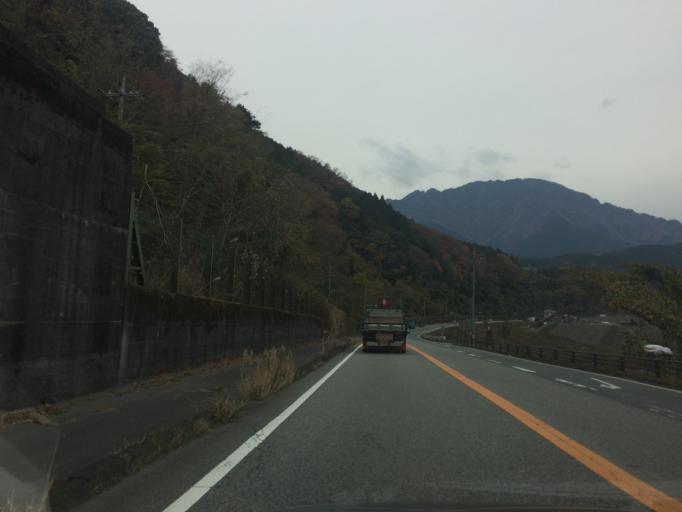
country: JP
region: Shizuoka
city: Fujinomiya
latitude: 35.2372
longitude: 138.4960
